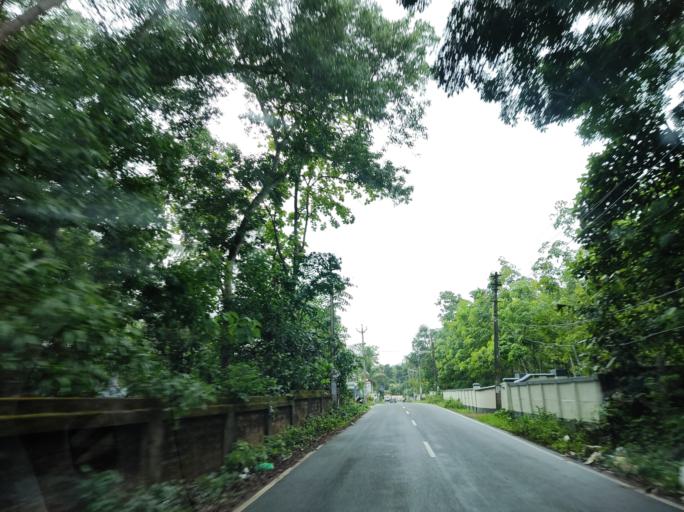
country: IN
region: Kerala
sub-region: Alappuzha
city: Mavelikara
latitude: 9.2351
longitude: 76.5605
